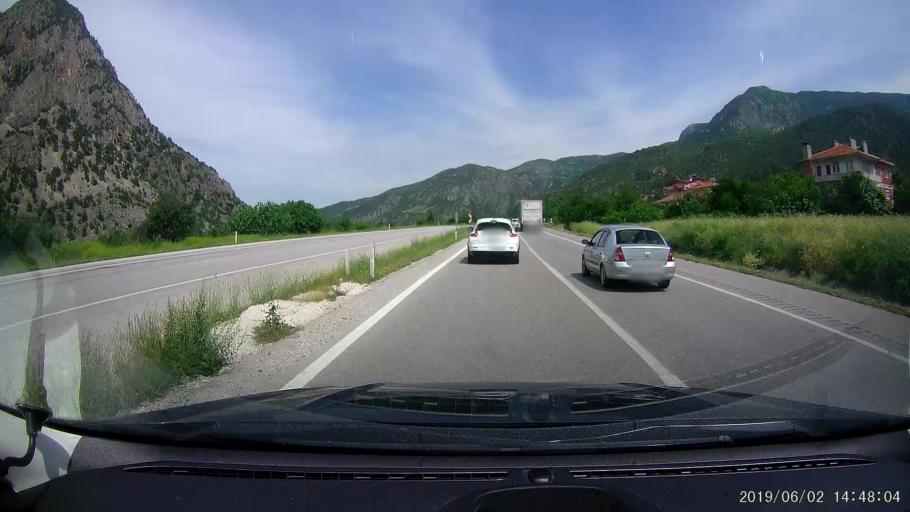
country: TR
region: Corum
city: Hacihamza
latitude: 41.0648
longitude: 34.4733
